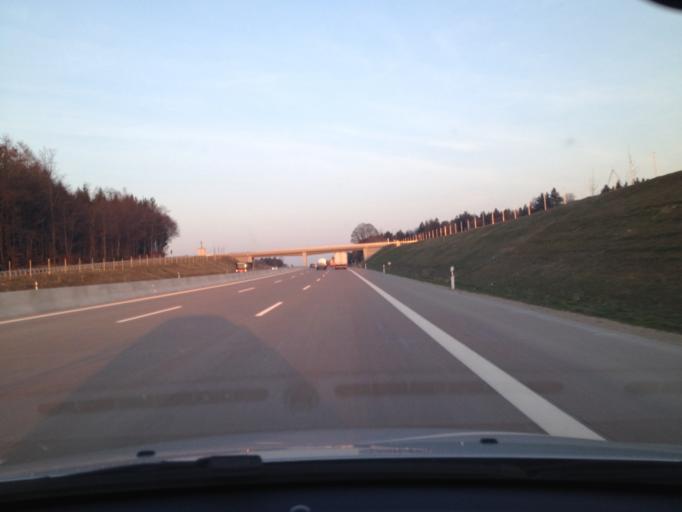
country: DE
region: Bavaria
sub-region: Swabia
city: Horgau
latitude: 48.4193
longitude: 10.6890
